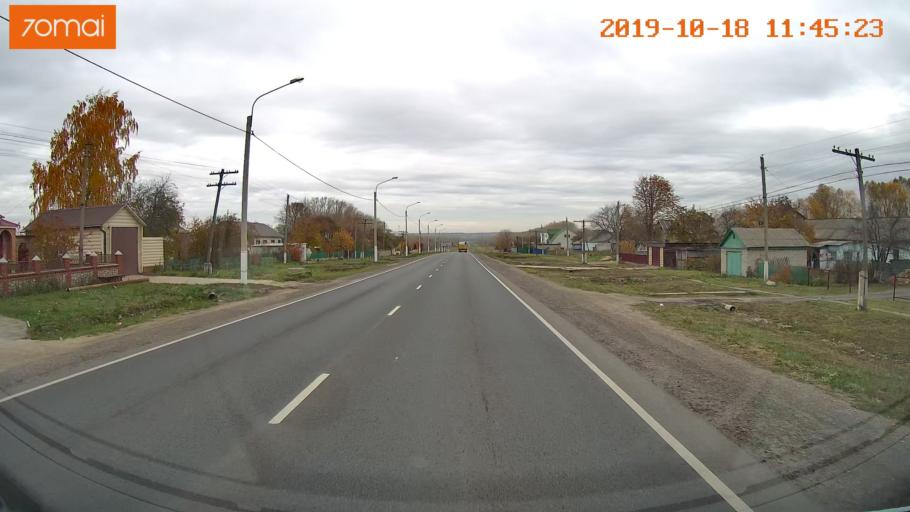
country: RU
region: Rjazan
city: Mikhaylov
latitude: 54.2101
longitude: 38.9694
